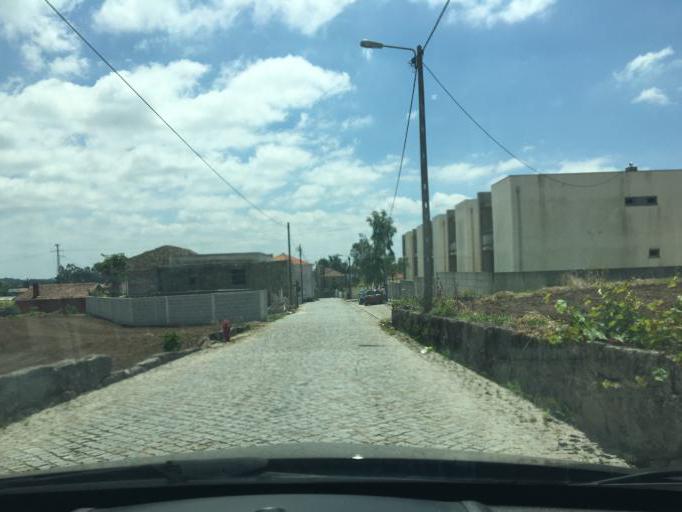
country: PT
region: Porto
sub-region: Maia
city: Anta
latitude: 41.2845
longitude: -8.6143
